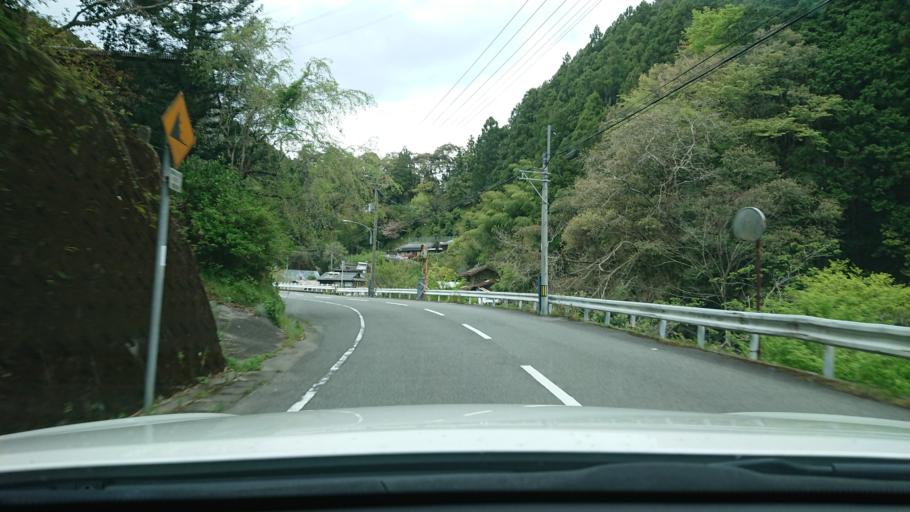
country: JP
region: Tokushima
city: Ishii
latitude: 33.9144
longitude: 134.4213
